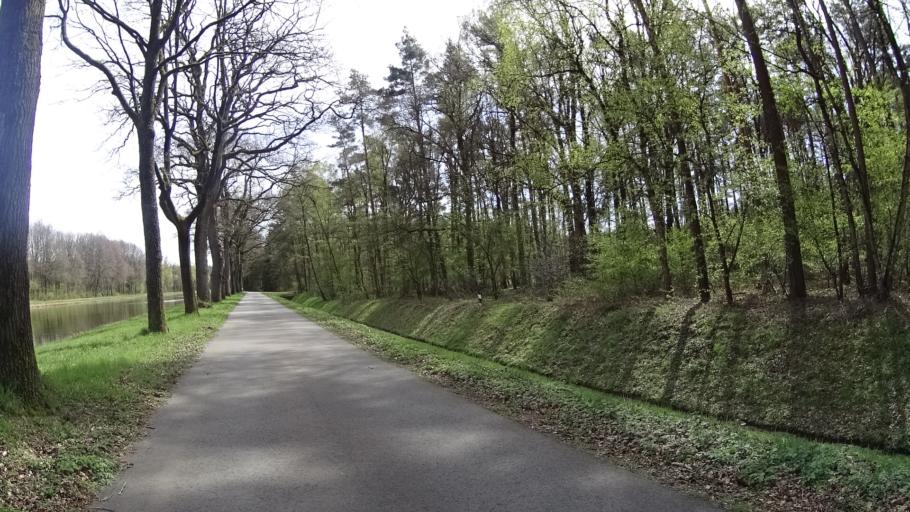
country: DE
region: Lower Saxony
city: Lunne
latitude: 52.4125
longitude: 7.3698
